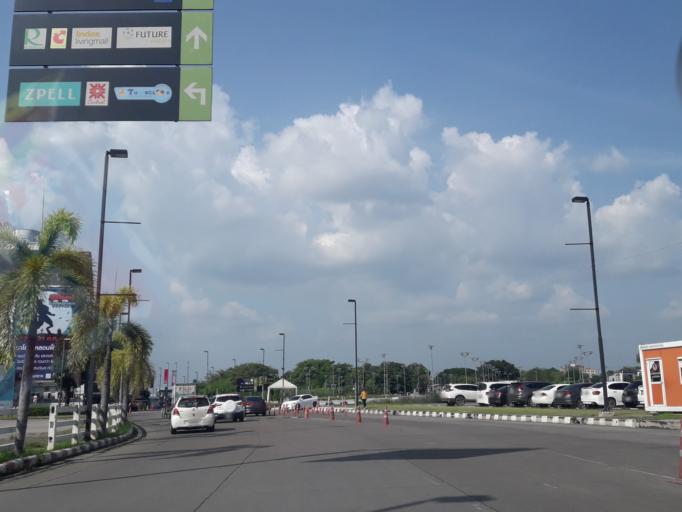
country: TH
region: Bangkok
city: Sai Mai
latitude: 13.9858
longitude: 100.6192
